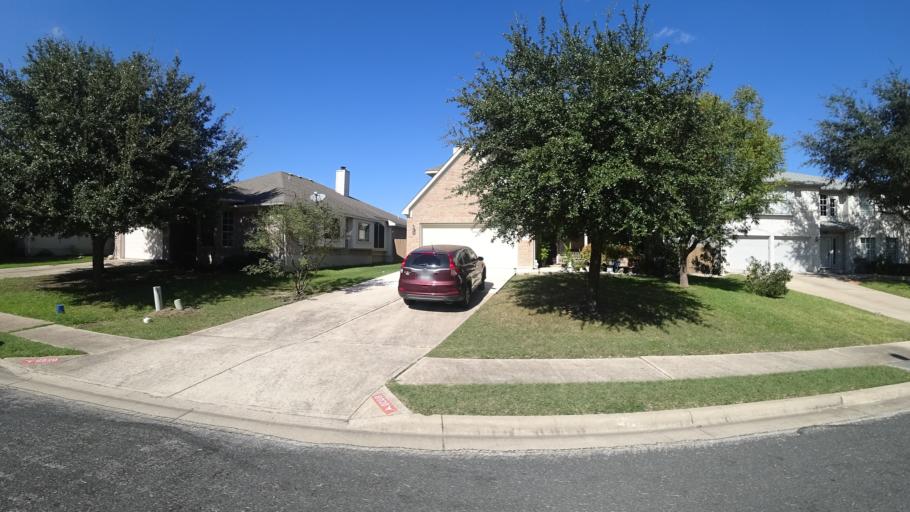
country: US
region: Texas
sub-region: Travis County
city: Manor
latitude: 30.3508
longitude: -97.6087
